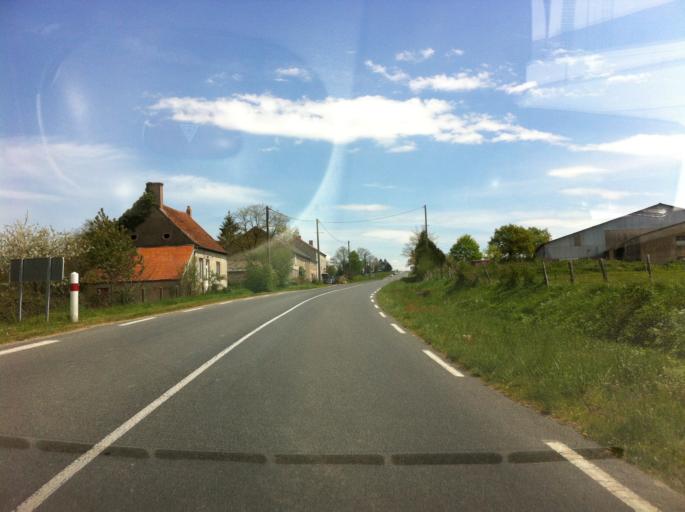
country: FR
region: Auvergne
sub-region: Departement de l'Allier
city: Chantelle
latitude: 46.3194
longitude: 3.1136
